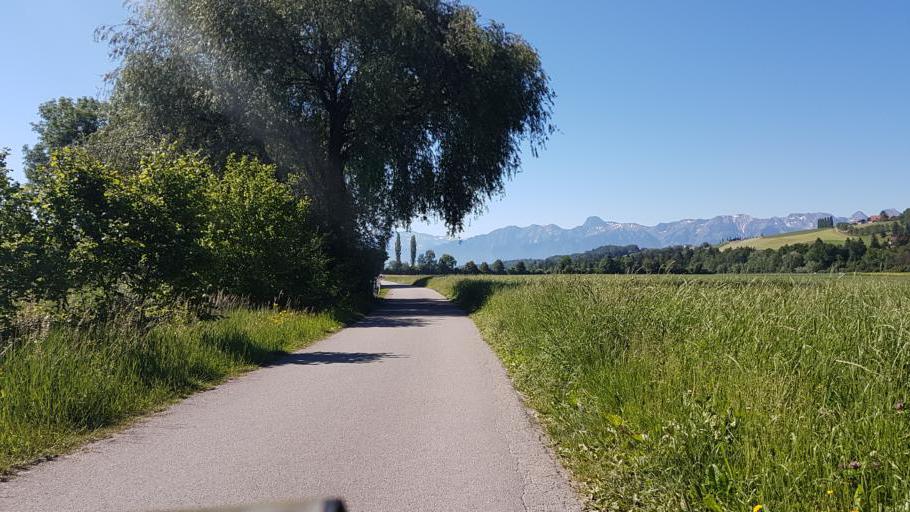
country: CH
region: Bern
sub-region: Bern-Mittelland District
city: Munsingen
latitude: 46.8620
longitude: 7.5586
